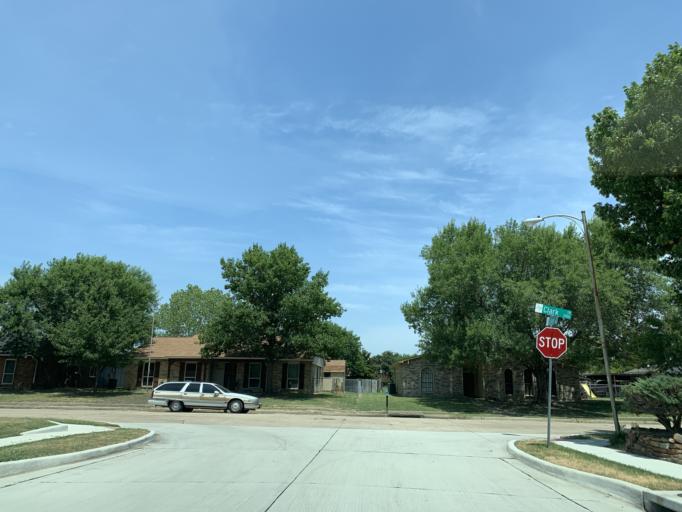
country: US
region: Texas
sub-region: Dallas County
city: Cedar Hill
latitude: 32.6487
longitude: -97.0345
